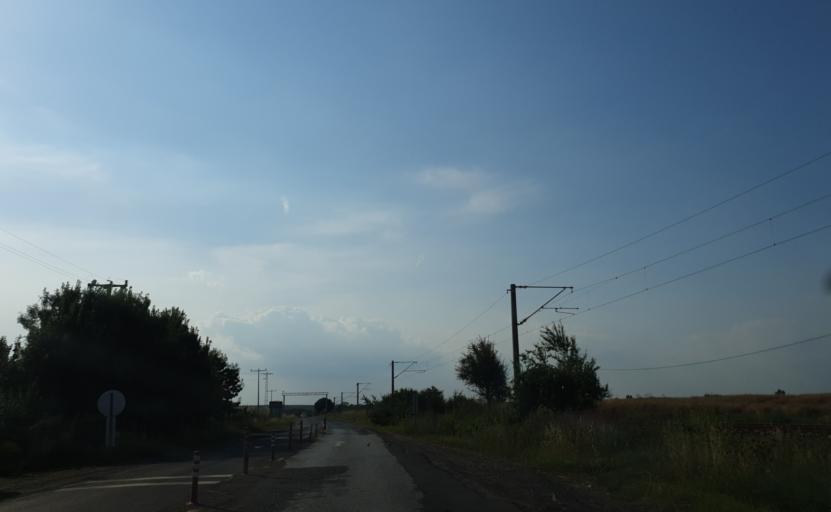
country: TR
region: Tekirdag
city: Muratli
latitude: 41.1788
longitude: 27.4880
